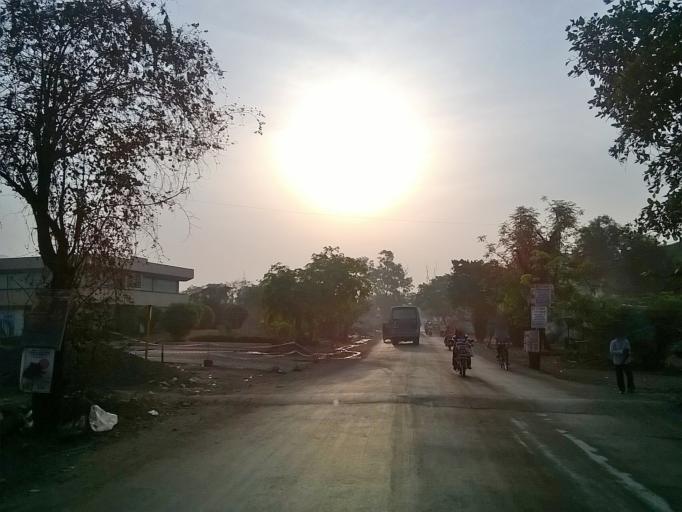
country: IN
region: Maharashtra
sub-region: Raigarh
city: Kalundri
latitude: 19.0006
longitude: 73.1338
